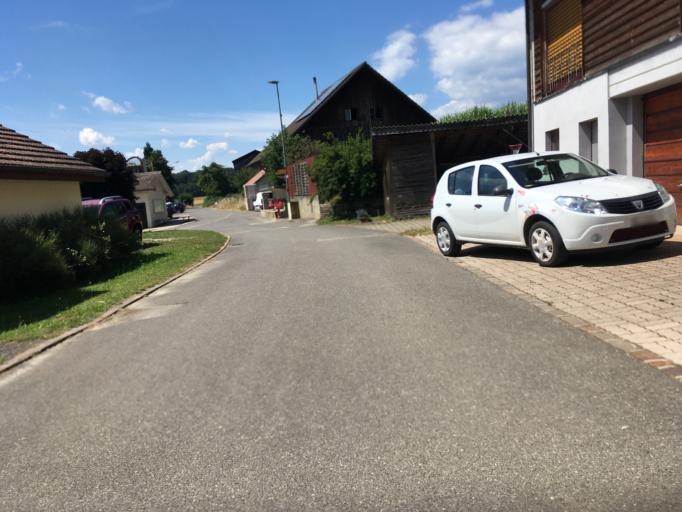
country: CH
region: Neuchatel
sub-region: Neuchatel District
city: Saint-Blaise
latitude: 46.9416
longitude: 6.9985
